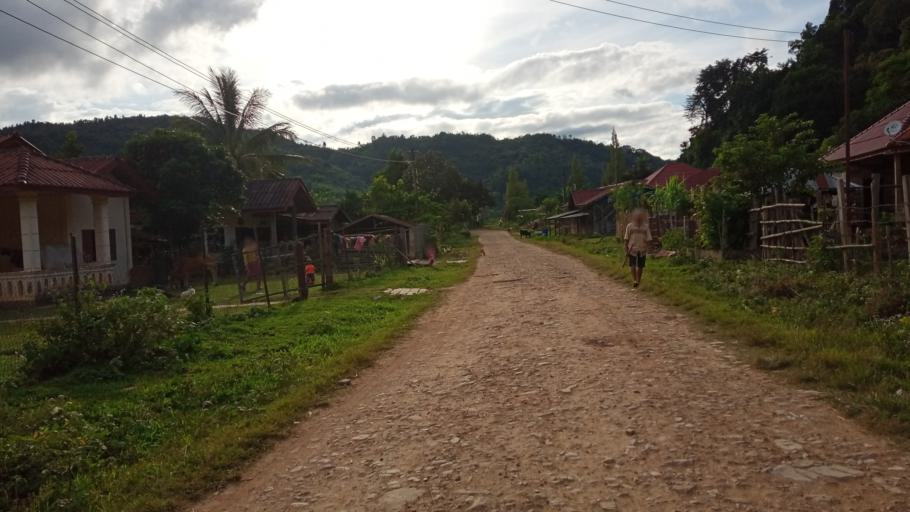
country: LA
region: Xiangkhoang
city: Phonsavan
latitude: 19.1102
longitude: 102.9245
